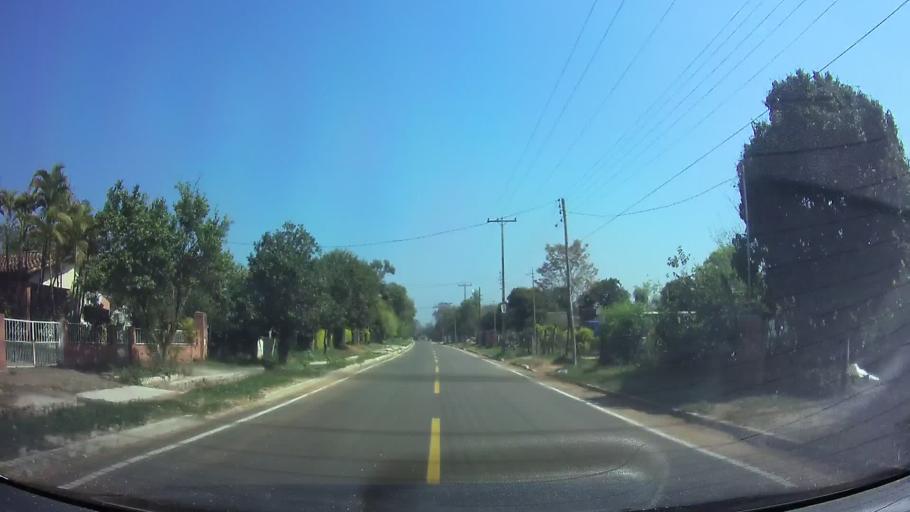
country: PY
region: Central
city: Limpio
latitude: -25.2223
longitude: -57.4866
